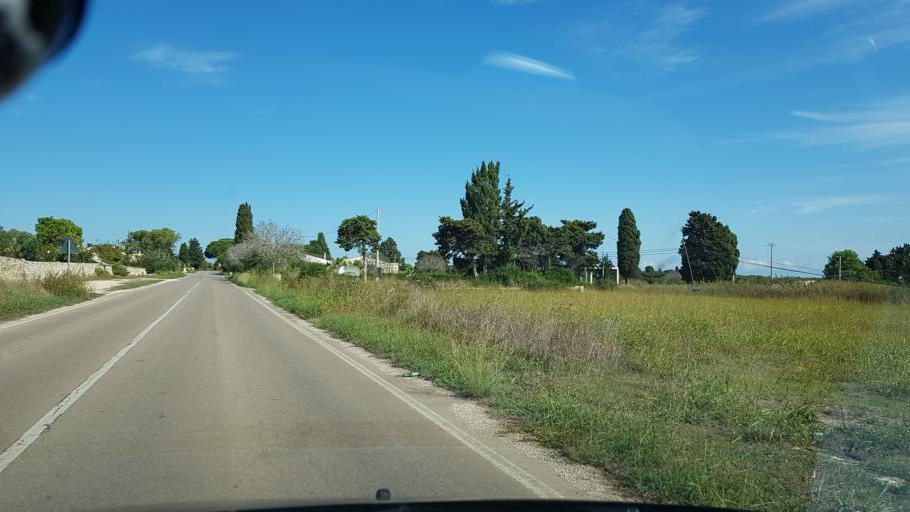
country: IT
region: Apulia
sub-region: Provincia di Lecce
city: Borgagne
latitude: 40.2317
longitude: 18.4436
